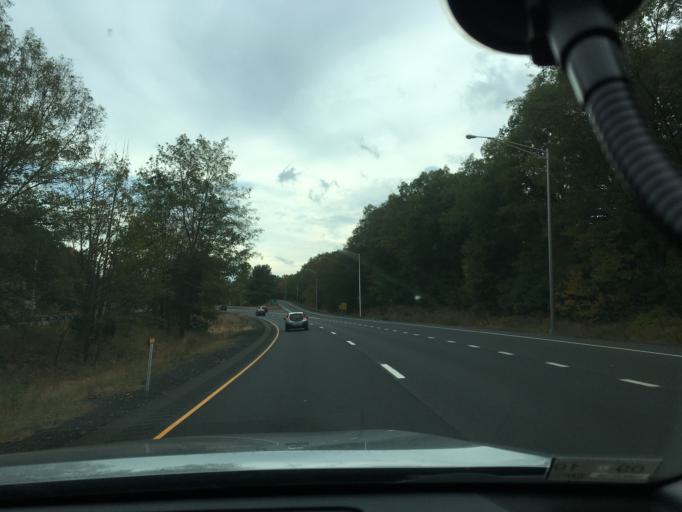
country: US
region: Connecticut
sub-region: Hartford County
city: Glastonbury Center
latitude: 41.6802
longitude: -72.5418
